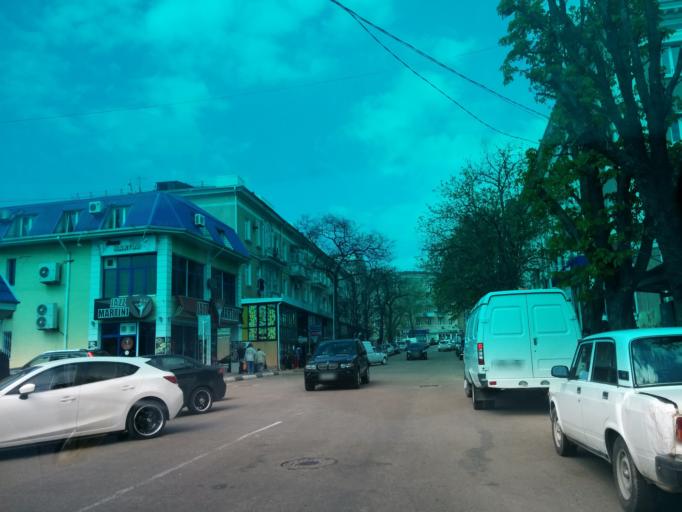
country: RU
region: Krasnodarskiy
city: Tuapse
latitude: 44.0986
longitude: 39.0805
